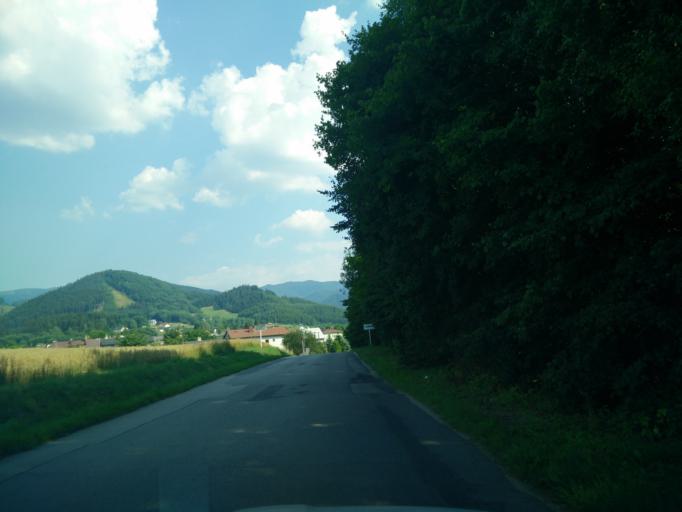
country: SK
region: Zilinsky
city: Rajec
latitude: 49.1033
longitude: 18.7015
